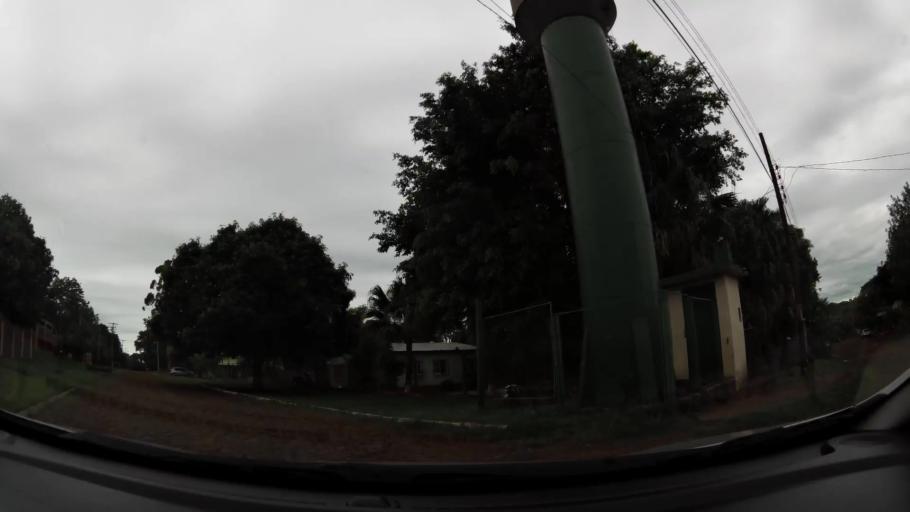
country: PY
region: Alto Parana
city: Ciudad del Este
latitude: -25.4396
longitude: -54.6413
